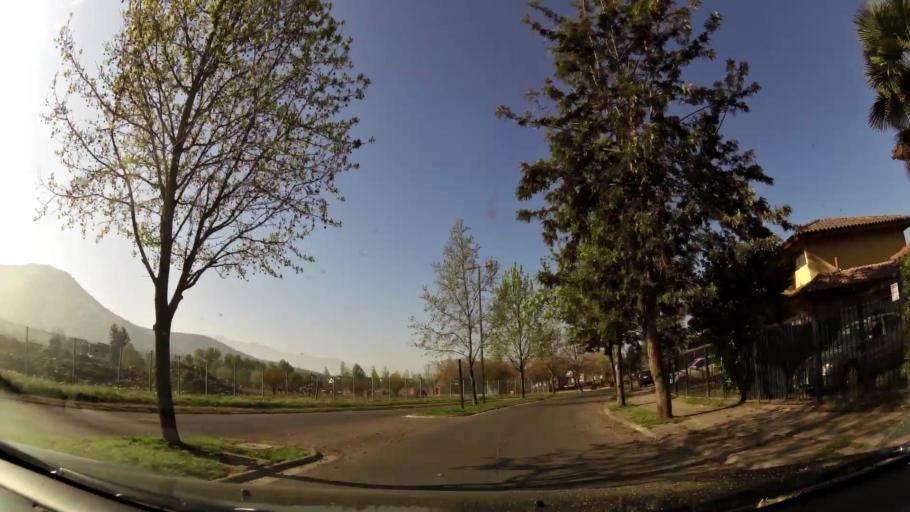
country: CL
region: Santiago Metropolitan
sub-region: Provincia de Chacabuco
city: Chicureo Abajo
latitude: -33.3565
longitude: -70.6655
